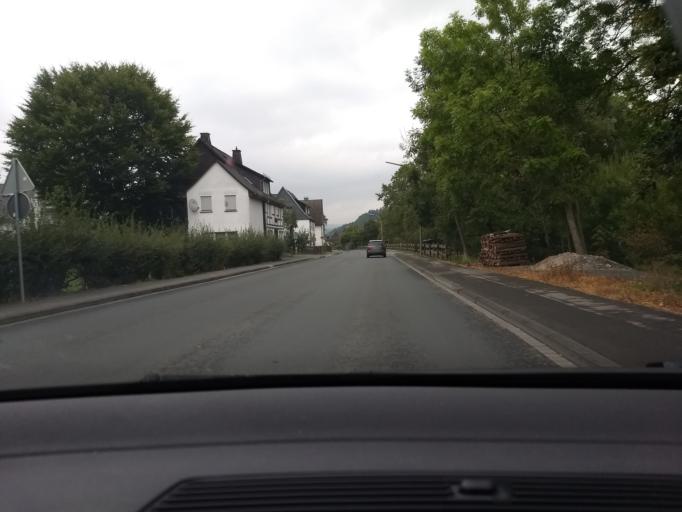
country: DE
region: North Rhine-Westphalia
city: Eslohe
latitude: 51.3353
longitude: 8.1631
